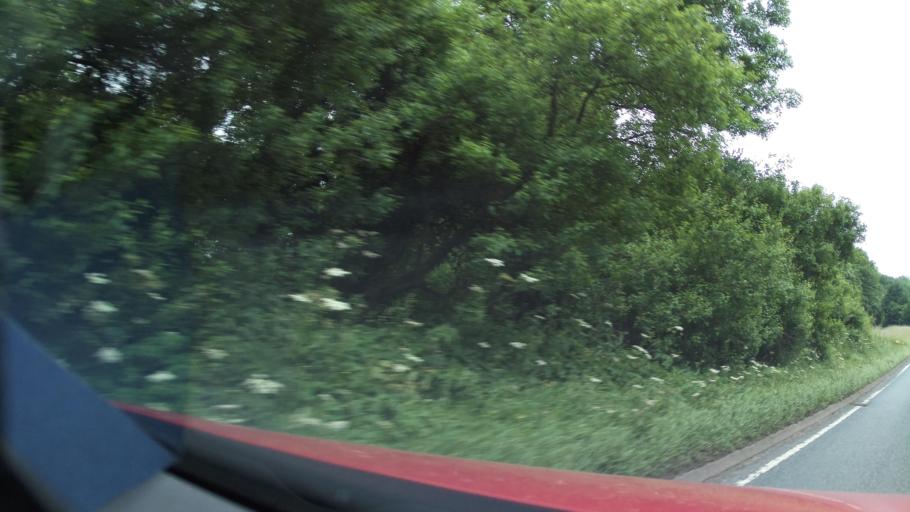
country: GB
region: England
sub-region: Staffordshire
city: Mayfield
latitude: 52.9965
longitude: -1.7497
